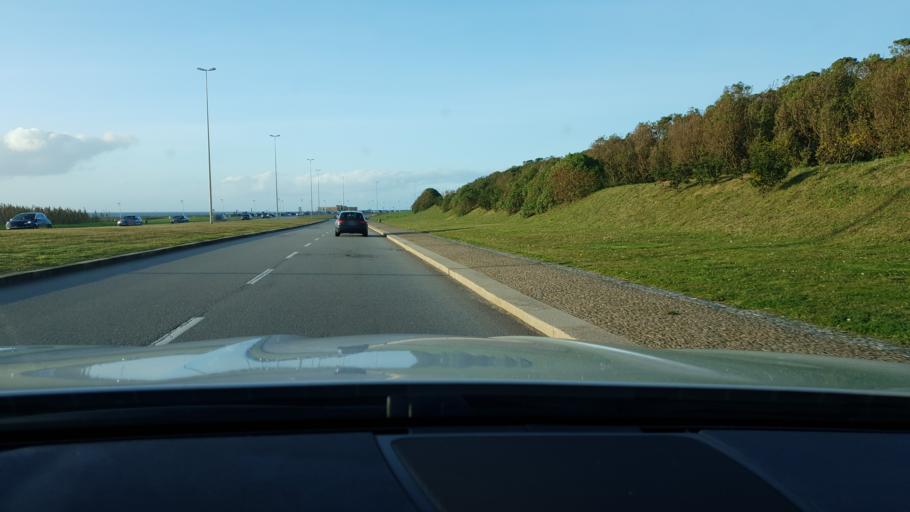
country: PT
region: Porto
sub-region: Matosinhos
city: Leca da Palmeira
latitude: 41.2039
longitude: -8.7130
